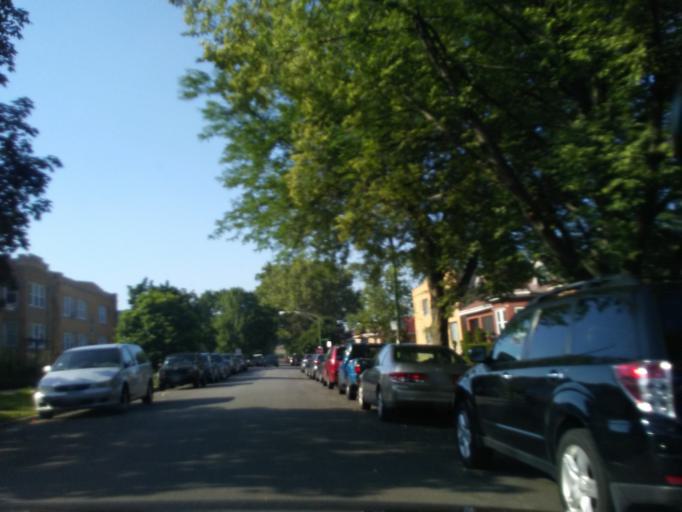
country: US
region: Illinois
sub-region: Cook County
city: Oak Park
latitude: 41.9342
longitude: -87.7381
